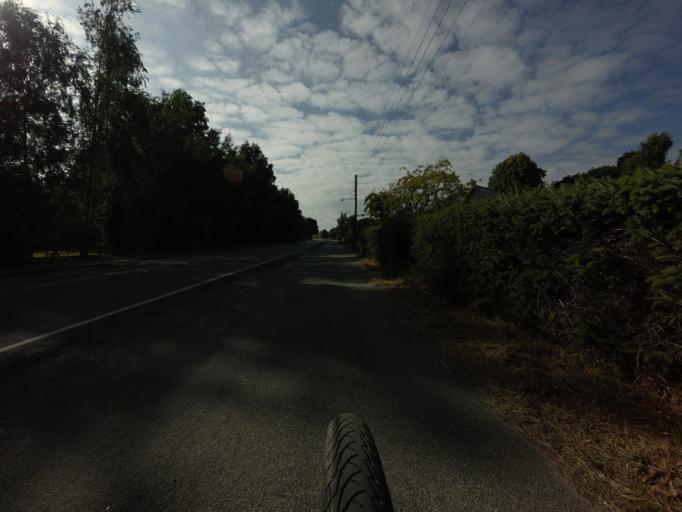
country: DK
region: North Denmark
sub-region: Laeso Kommune
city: Byrum
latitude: 57.2853
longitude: 10.9309
